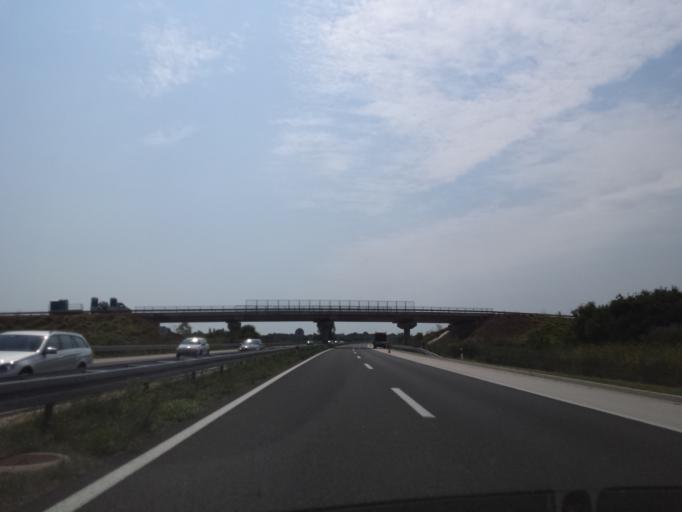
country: HR
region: Zadarska
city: Posedarje
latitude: 44.2028
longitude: 15.4438
